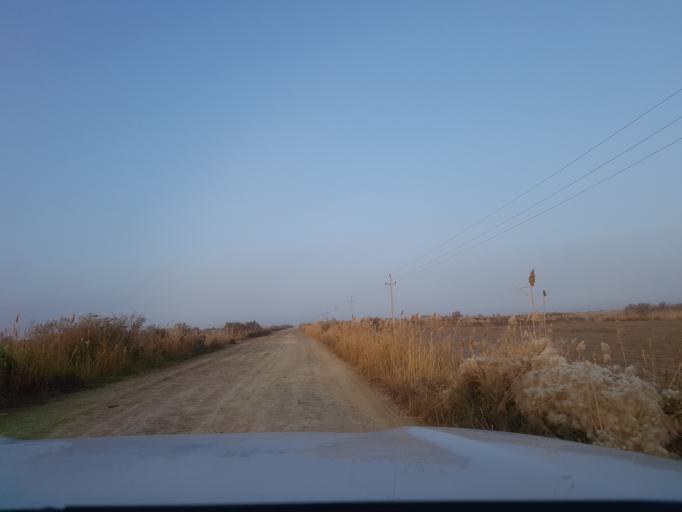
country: TM
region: Dasoguz
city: Koeneuergench
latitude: 41.8461
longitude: 58.3863
